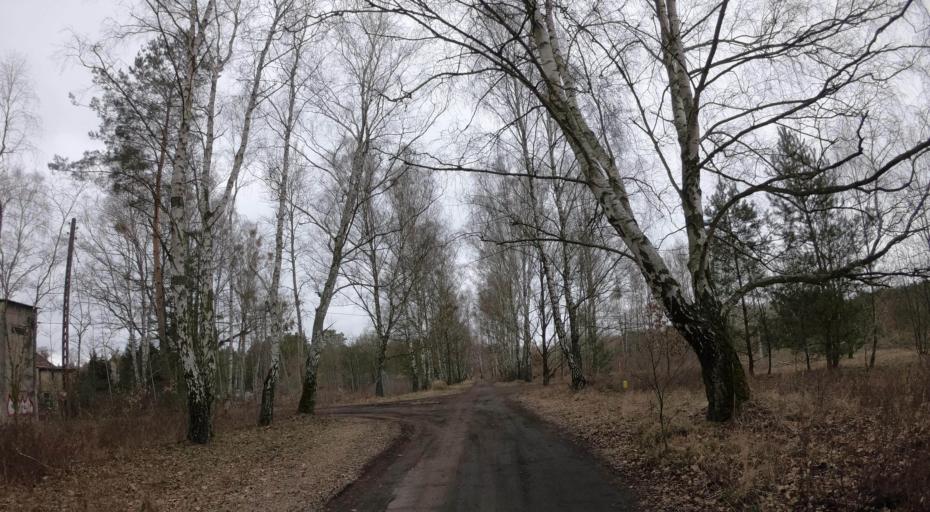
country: PL
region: West Pomeranian Voivodeship
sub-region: Powiat policki
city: Police
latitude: 53.6616
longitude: 14.4847
